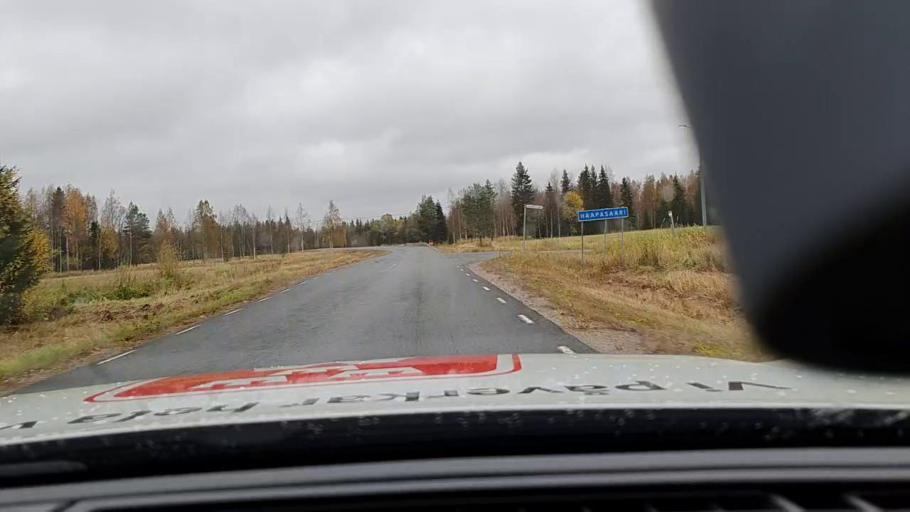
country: SE
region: Norrbotten
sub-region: Haparanda Kommun
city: Haparanda
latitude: 65.9321
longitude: 23.8156
